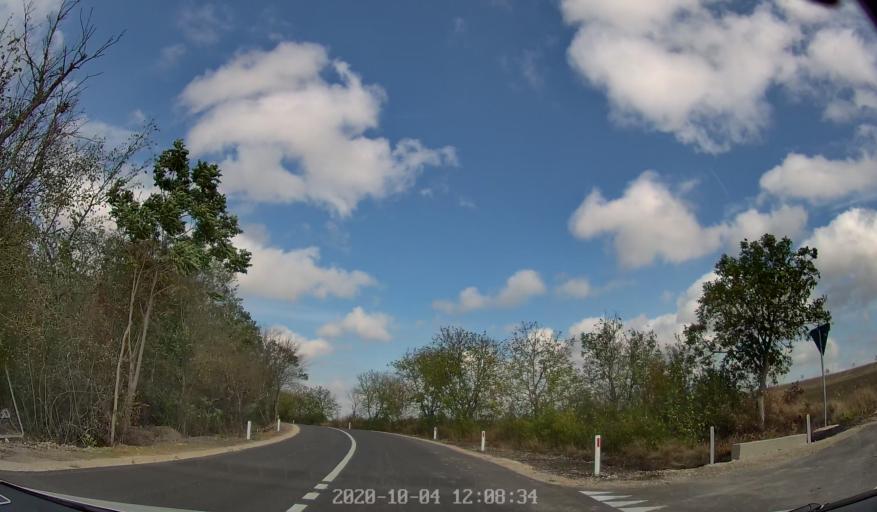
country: MD
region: Rezina
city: Saharna
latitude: 47.5959
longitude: 28.9769
